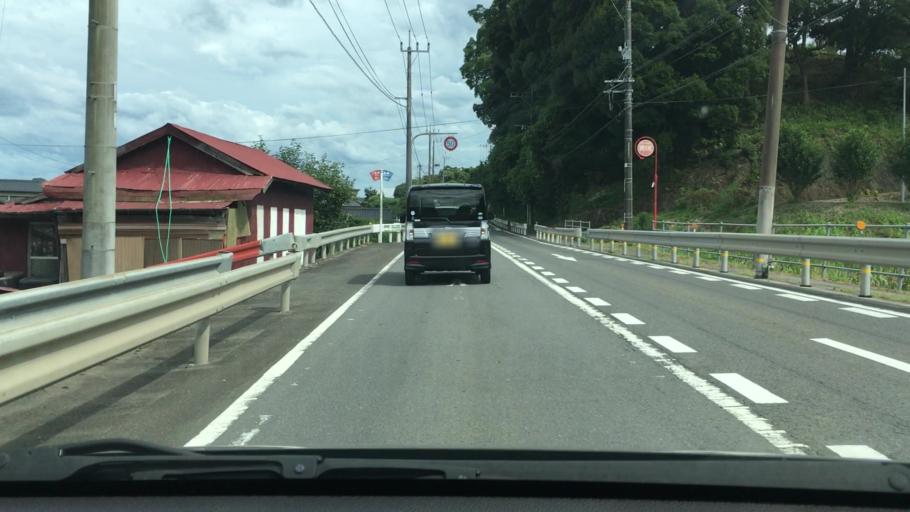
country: JP
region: Nagasaki
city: Togitsu
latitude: 32.9382
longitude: 129.7823
